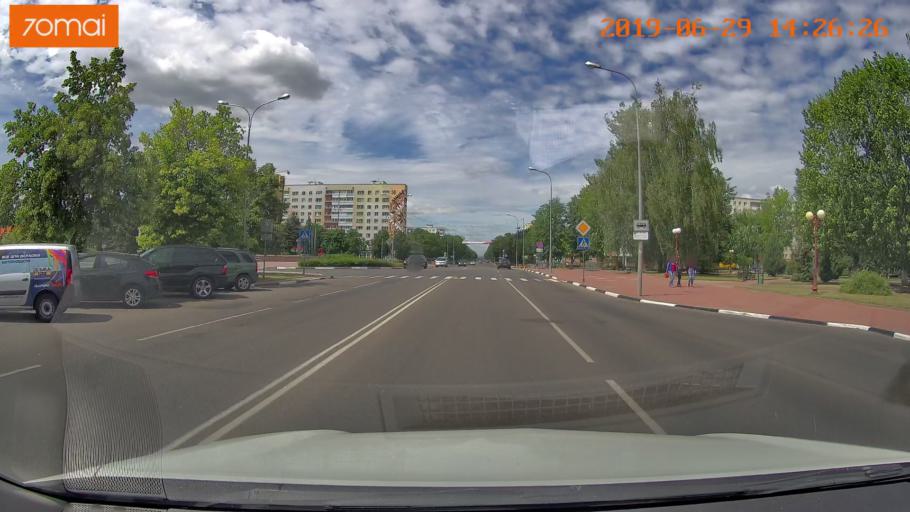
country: BY
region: Minsk
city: Salihorsk
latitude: 52.7828
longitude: 27.5418
